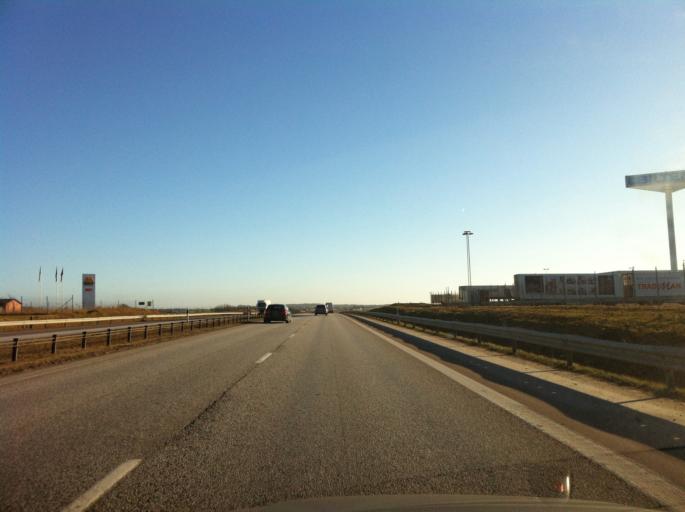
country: SE
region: Skane
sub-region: Angelholms Kommun
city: AEngelholm
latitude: 56.2453
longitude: 12.8987
